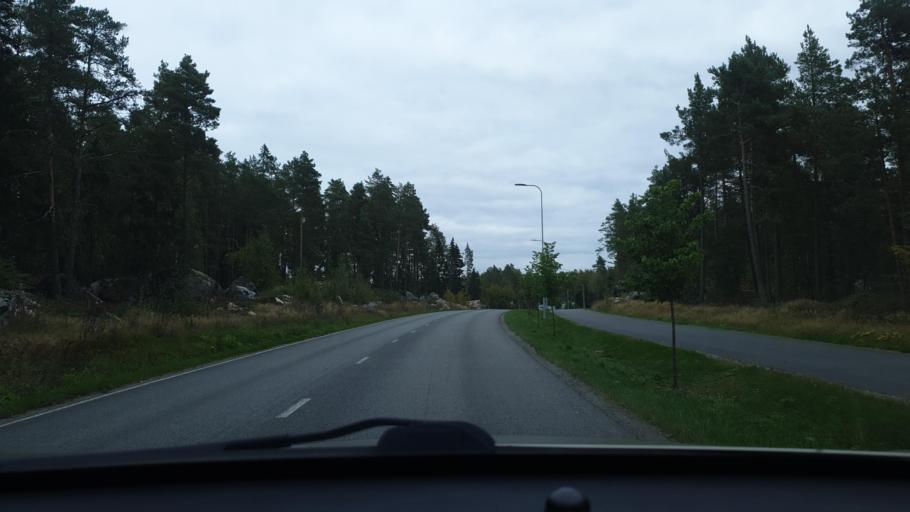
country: FI
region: Ostrobothnia
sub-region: Vaasa
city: Korsholm
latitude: 63.1206
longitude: 21.6496
